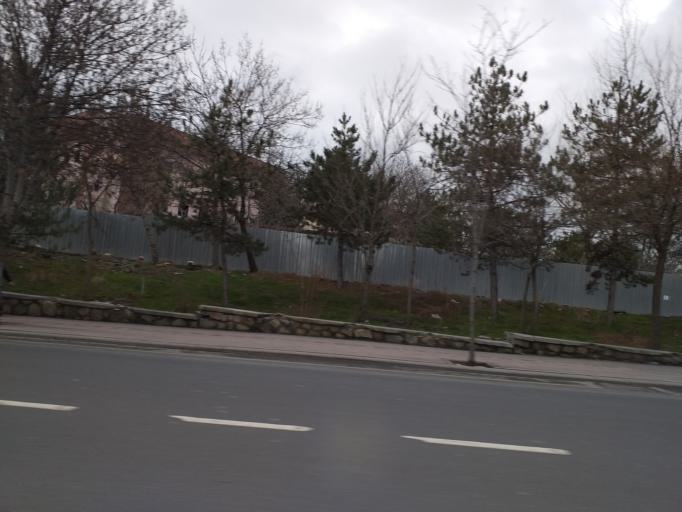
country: TR
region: Ankara
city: Ankara
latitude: 39.9680
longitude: 32.8374
